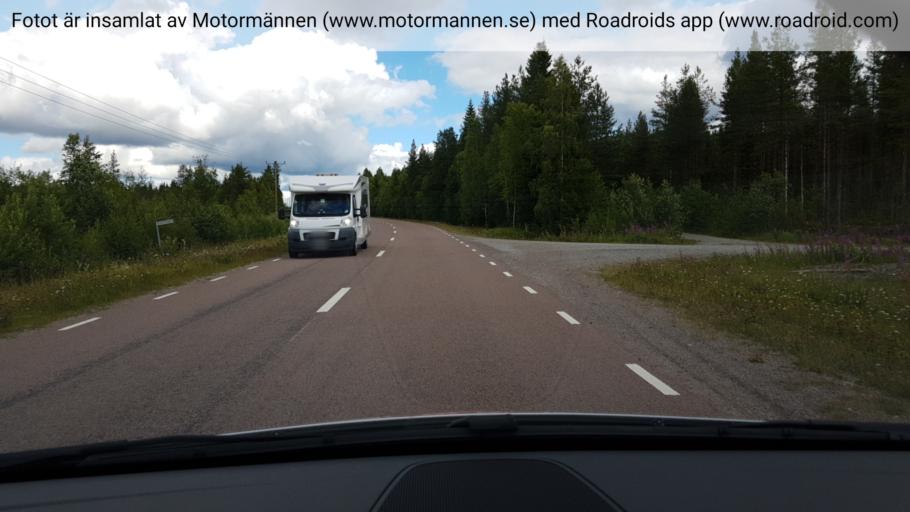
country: SE
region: Jaemtland
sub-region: Braecke Kommun
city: Braecke
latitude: 62.9172
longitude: 15.6786
